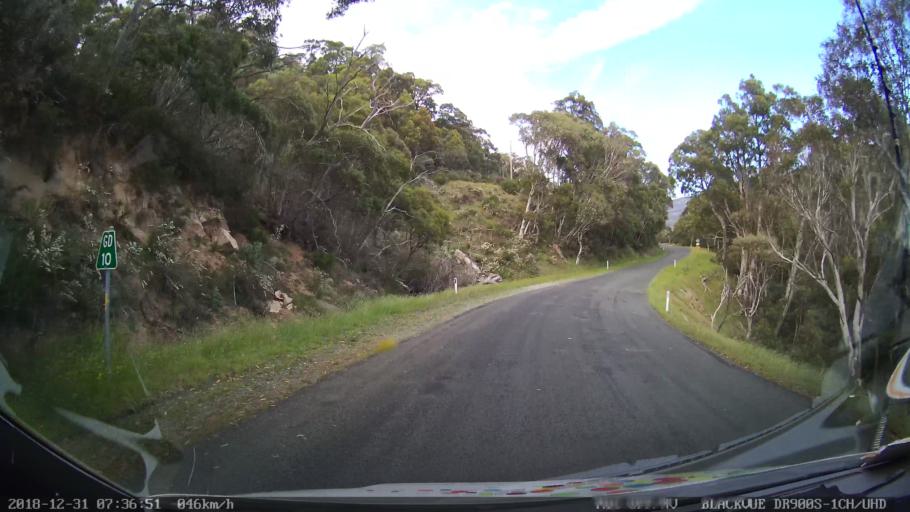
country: AU
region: New South Wales
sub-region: Snowy River
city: Jindabyne
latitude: -36.3433
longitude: 148.4409
